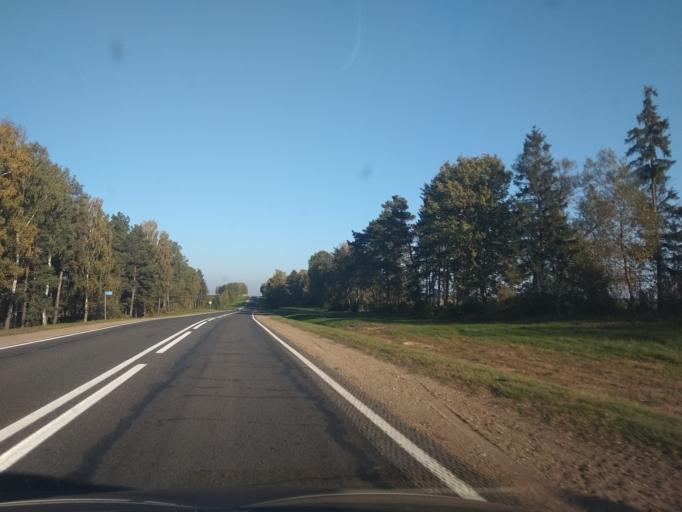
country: BY
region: Grodnenskaya
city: Svislach
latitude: 53.1262
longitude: 24.1249
